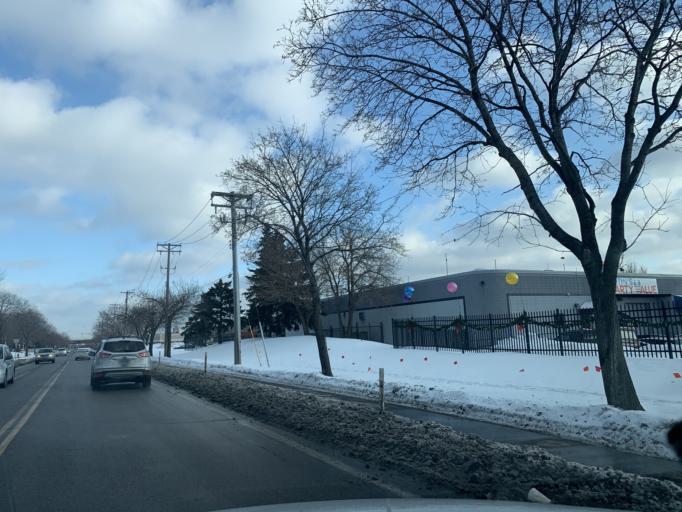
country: US
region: Minnesota
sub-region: Hennepin County
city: Minneapolis
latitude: 44.9920
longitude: -93.2926
